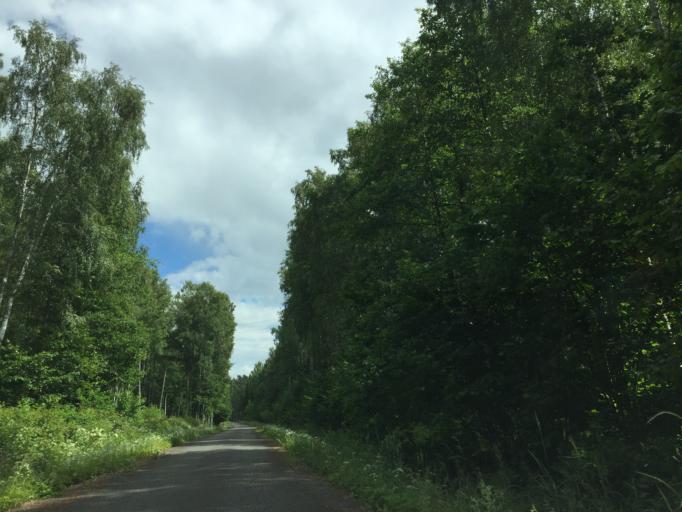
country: LV
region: Saulkrastu
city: Saulkrasti
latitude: 57.3497
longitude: 24.4240
